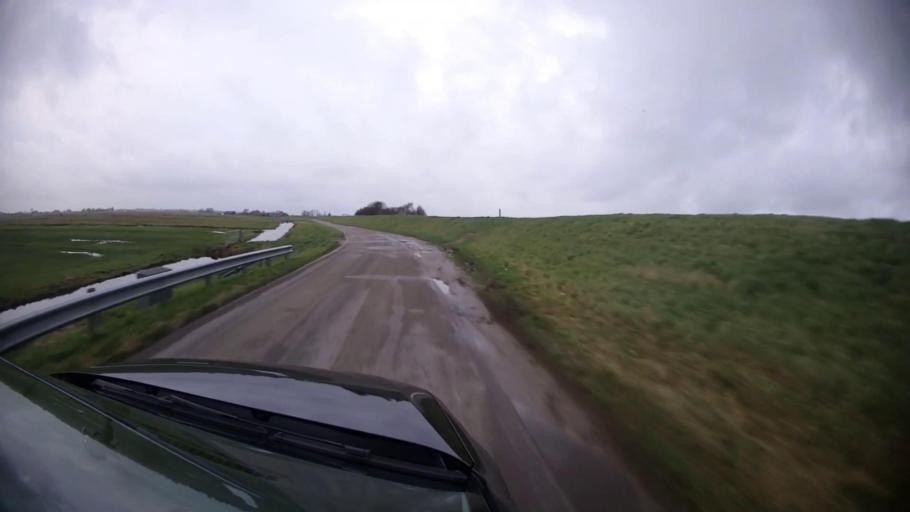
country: NL
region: North Holland
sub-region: Gemeente Waterland
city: Marken
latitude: 52.4229
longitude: 5.0728
